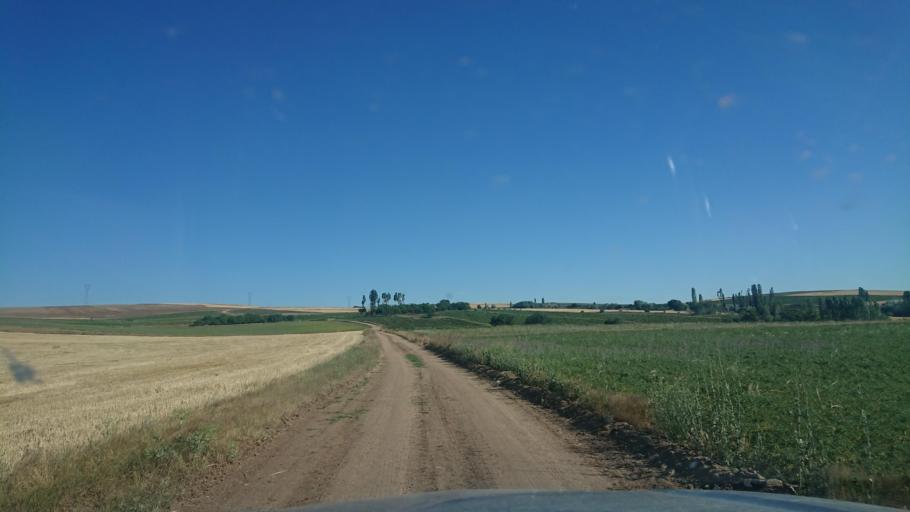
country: TR
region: Aksaray
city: Agacoren
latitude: 38.8283
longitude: 33.9535
